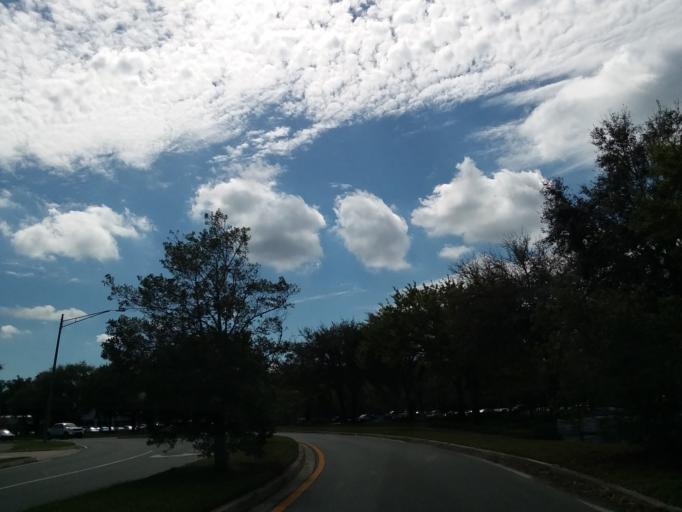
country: US
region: Florida
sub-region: Saint Johns County
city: Fruit Cove
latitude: 30.1670
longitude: -81.6030
